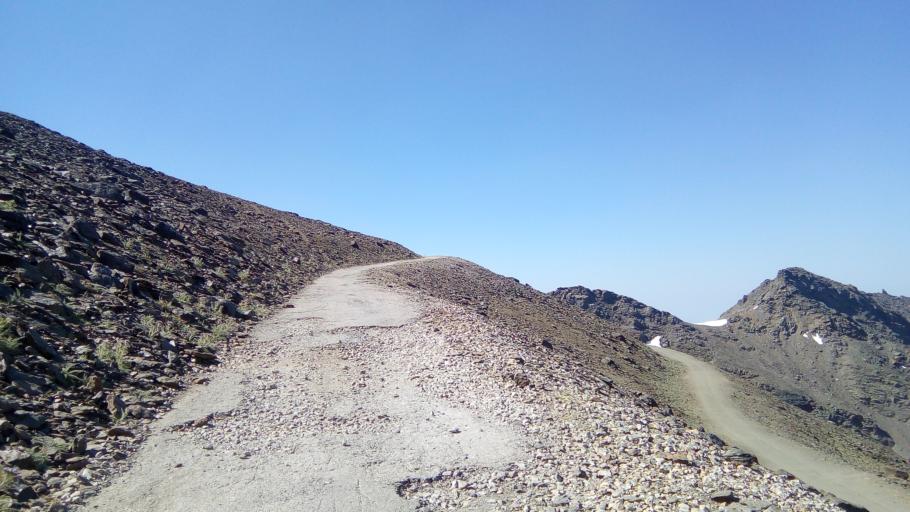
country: ES
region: Andalusia
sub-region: Provincia de Granada
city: Capileira
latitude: 37.0535
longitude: -3.3712
